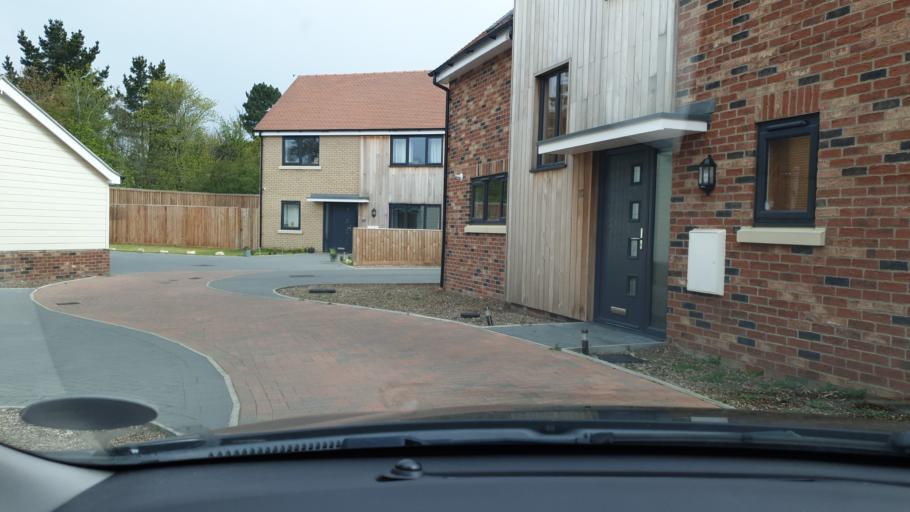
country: GB
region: England
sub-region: Suffolk
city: East Bergholt
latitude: 51.9220
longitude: 0.9868
